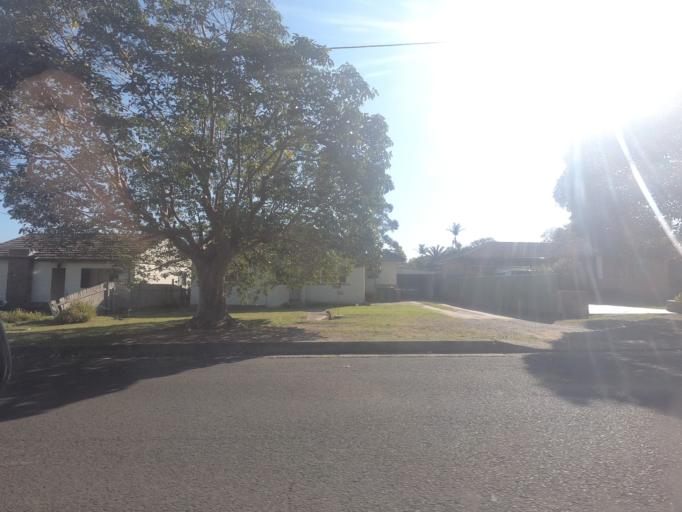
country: AU
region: New South Wales
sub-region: Wollongong
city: Koonawarra
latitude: -34.4921
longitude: 150.7992
